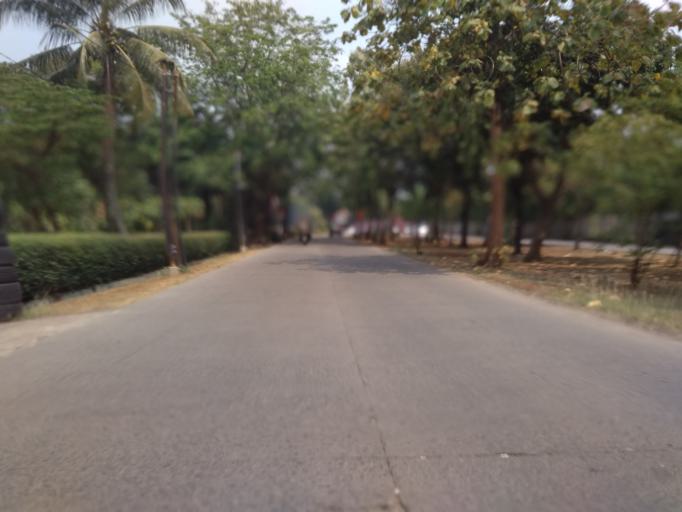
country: ID
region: West Java
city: Pamulang
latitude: -6.3154
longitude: 106.7899
